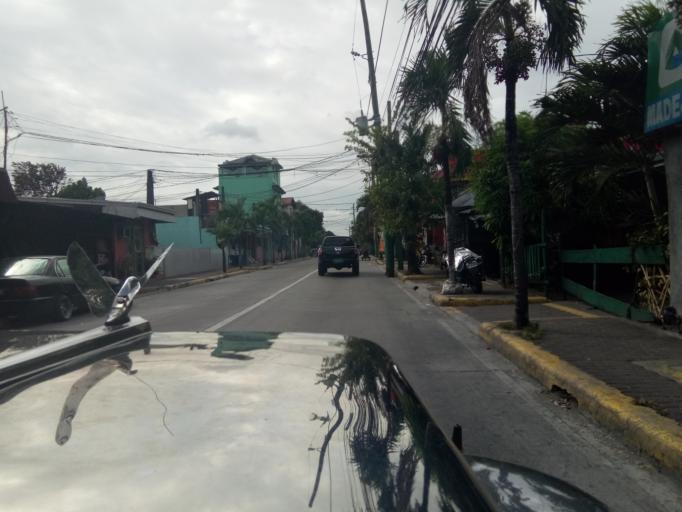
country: PH
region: Calabarzon
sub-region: Province of Cavite
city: Dasmarinas
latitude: 14.3209
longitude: 120.9396
